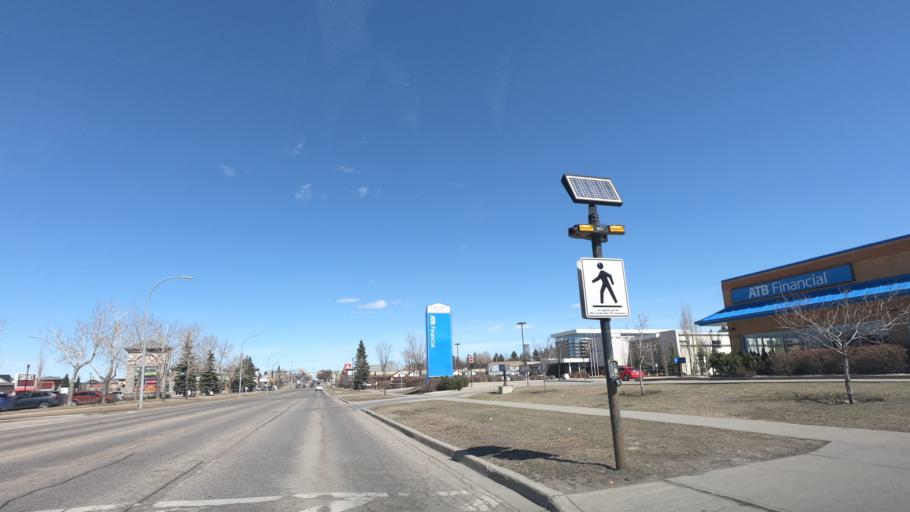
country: CA
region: Alberta
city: Airdrie
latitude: 51.2876
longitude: -114.0133
